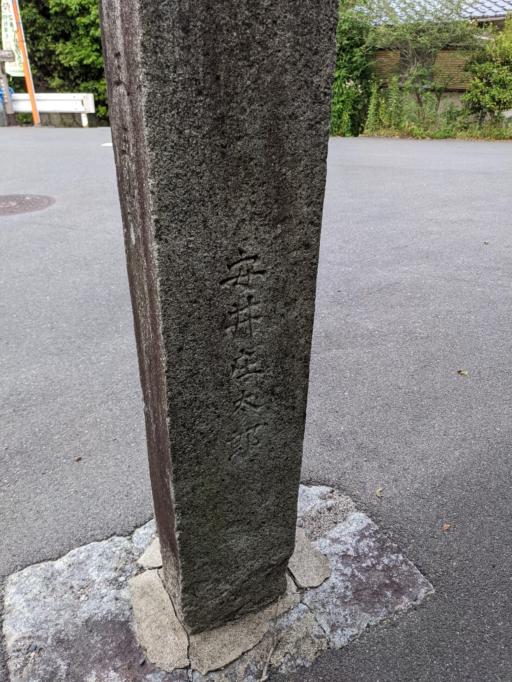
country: JP
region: Kyoto
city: Muko
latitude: 34.9566
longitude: 135.6587
